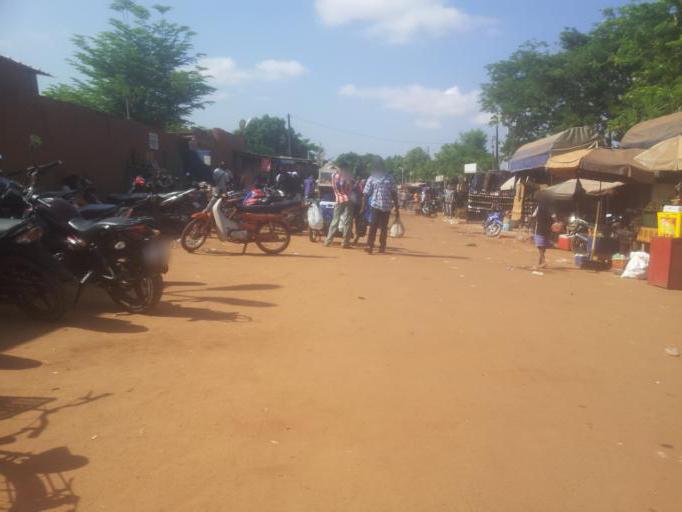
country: BF
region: Centre
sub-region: Kadiogo Province
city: Ouagadougou
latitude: 12.3627
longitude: -1.5404
